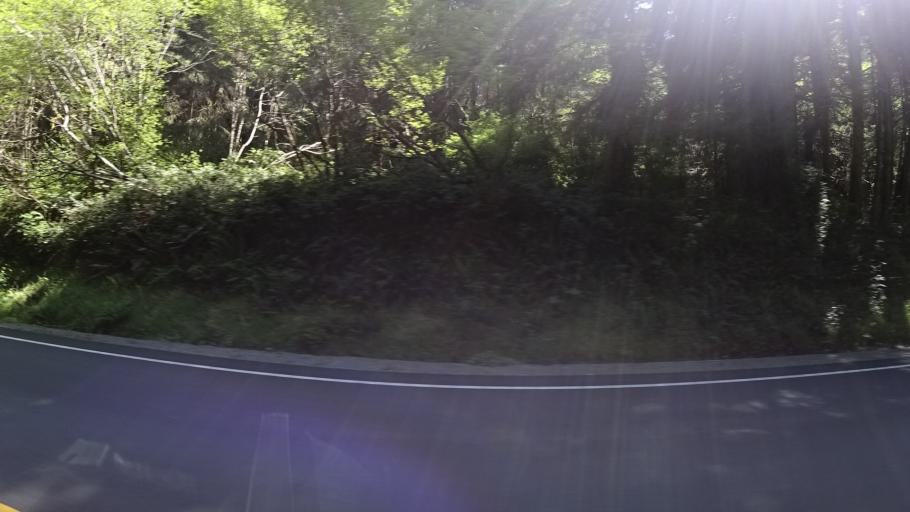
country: US
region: California
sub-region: Humboldt County
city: Westhaven-Moonstone
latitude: 41.1738
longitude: -124.1022
